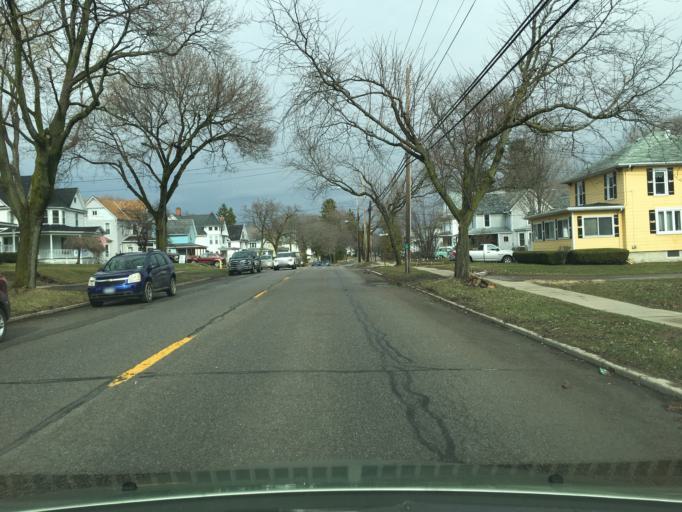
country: US
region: New York
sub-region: Wyoming County
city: Perry
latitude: 42.7250
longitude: -77.9953
